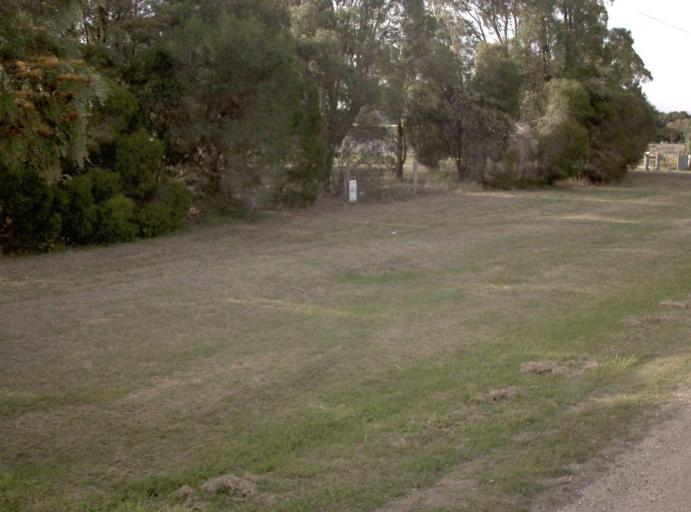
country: AU
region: Victoria
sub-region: Wellington
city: Sale
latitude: -37.9485
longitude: 146.9885
